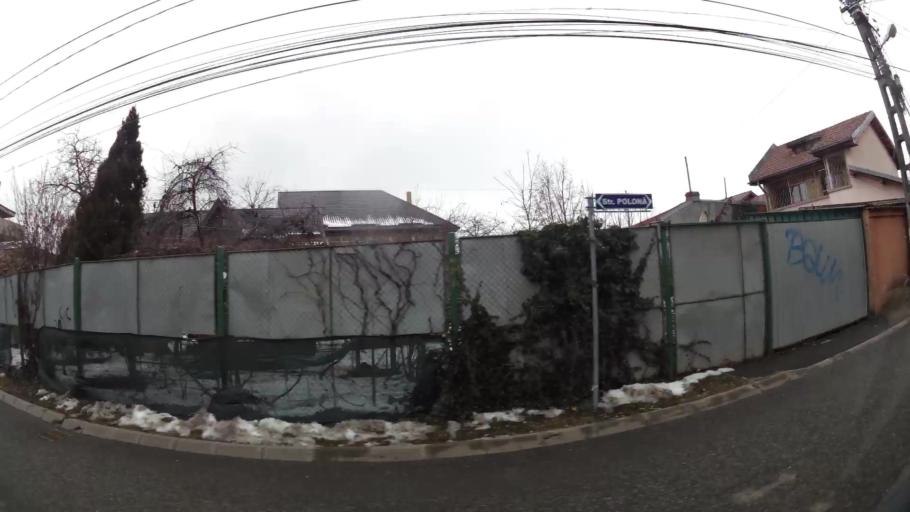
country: RO
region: Ilfov
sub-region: Comuna Otopeni
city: Otopeni
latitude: 44.5472
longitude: 26.0767
